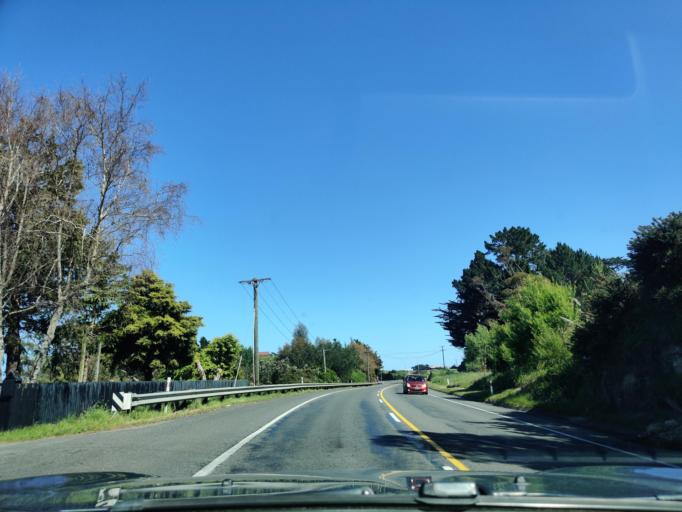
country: NZ
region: Manawatu-Wanganui
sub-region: Wanganui District
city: Wanganui
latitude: -39.9585
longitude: 175.0836
